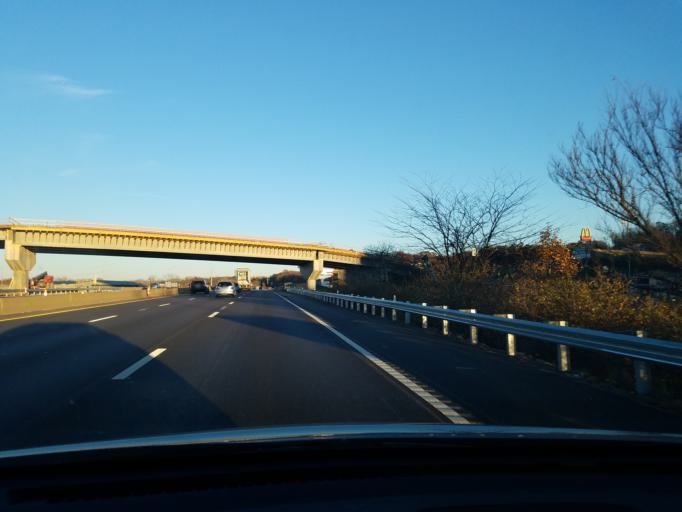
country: US
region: Missouri
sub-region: Saint Louis County
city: Valley Park
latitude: 38.5389
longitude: -90.4975
